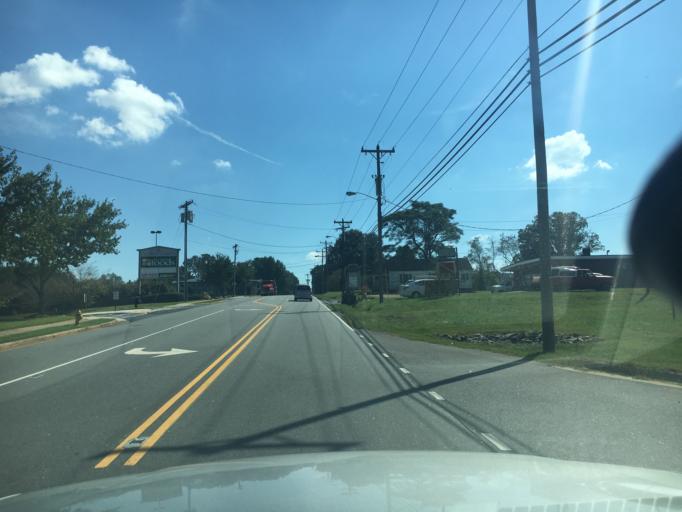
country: US
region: North Carolina
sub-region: Catawba County
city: Claremont
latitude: 35.7208
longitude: -81.1566
